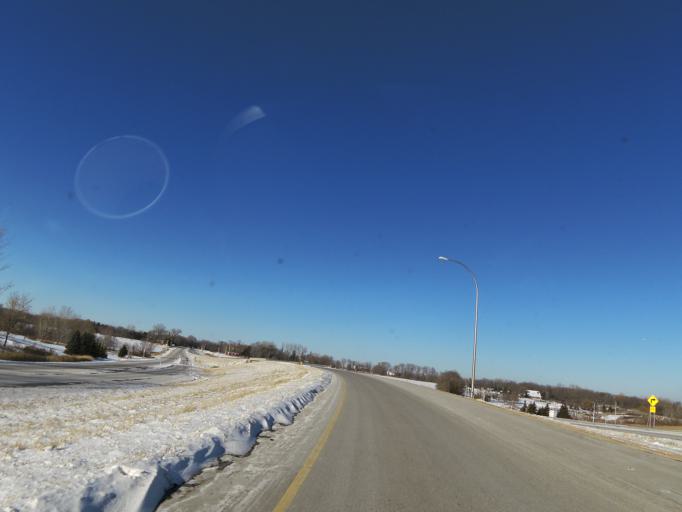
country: US
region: Minnesota
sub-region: Scott County
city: Shakopee
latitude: 44.7446
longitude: -93.4999
